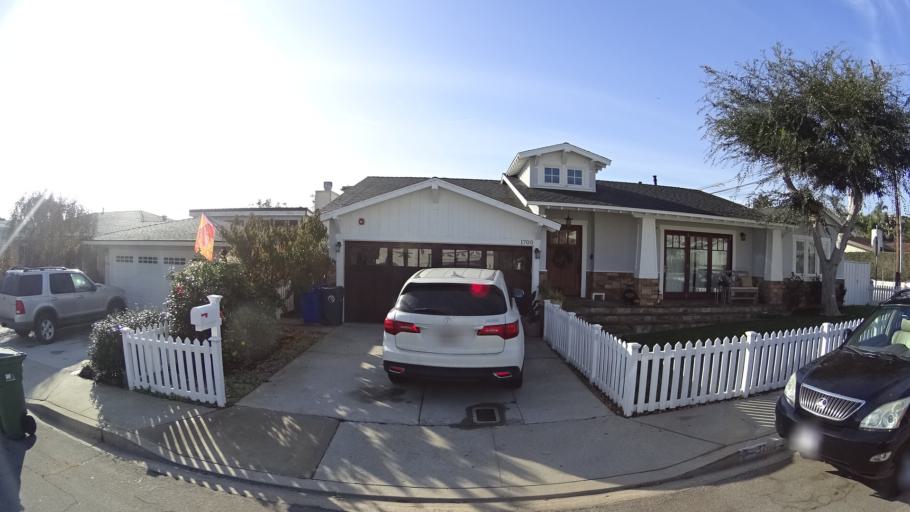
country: US
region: California
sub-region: Los Angeles County
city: Hermosa Beach
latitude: 33.8828
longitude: -118.3828
